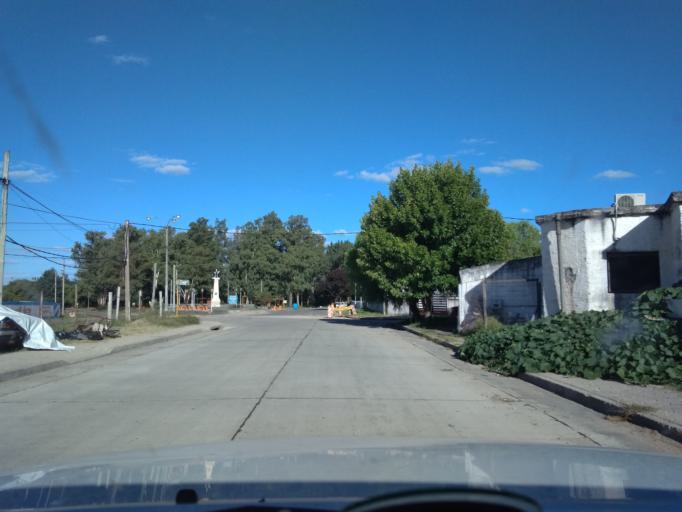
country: UY
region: Florida
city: Florida
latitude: -34.0925
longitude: -56.2097
